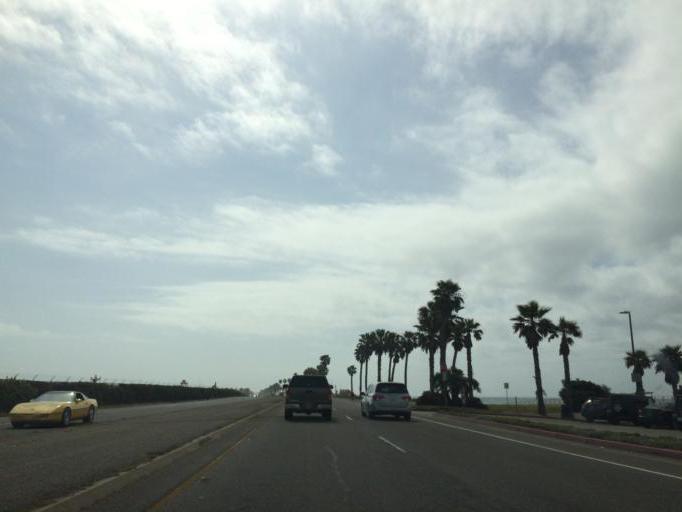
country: US
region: California
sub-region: Orange County
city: Huntington Beach
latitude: 33.6737
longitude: -118.0248
